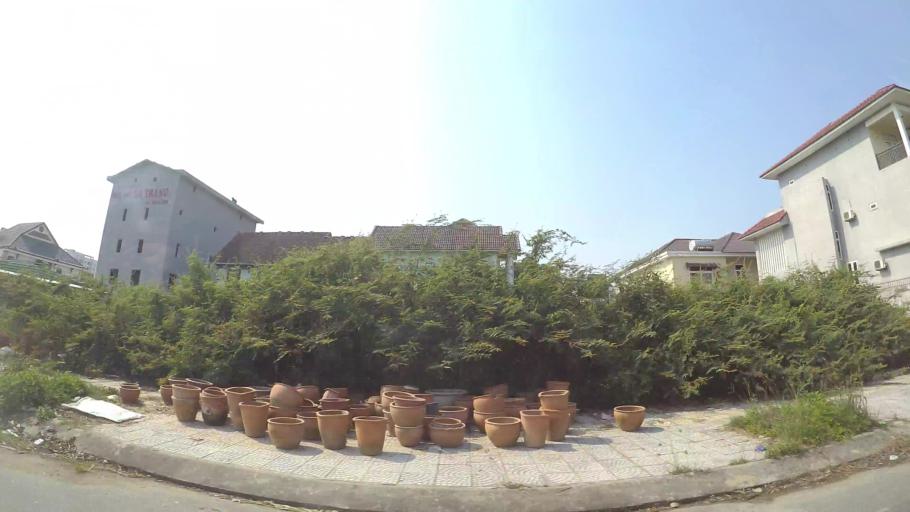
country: VN
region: Da Nang
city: Cam Le
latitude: 16.0075
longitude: 108.2004
